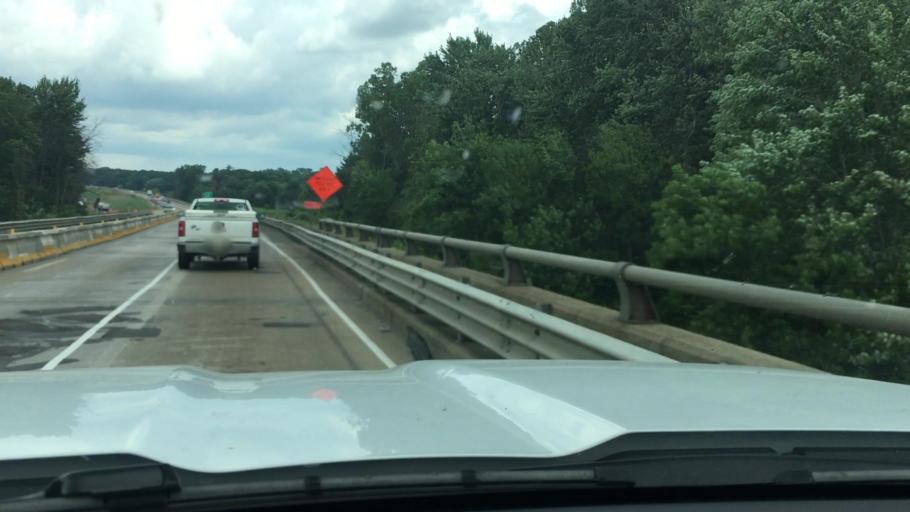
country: US
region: Michigan
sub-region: Kent County
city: Rockford
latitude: 43.1531
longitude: -85.5820
